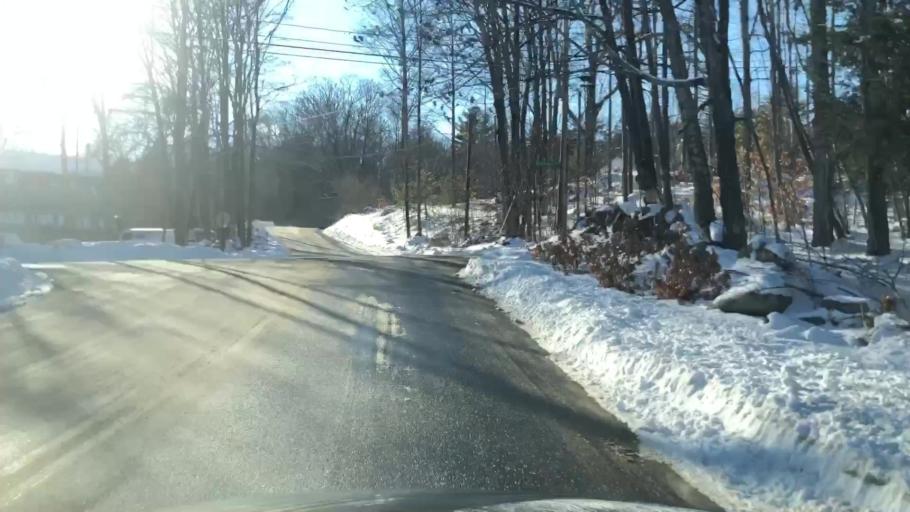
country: US
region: New Hampshire
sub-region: Hillsborough County
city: Wilton
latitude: 42.8174
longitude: -71.7224
